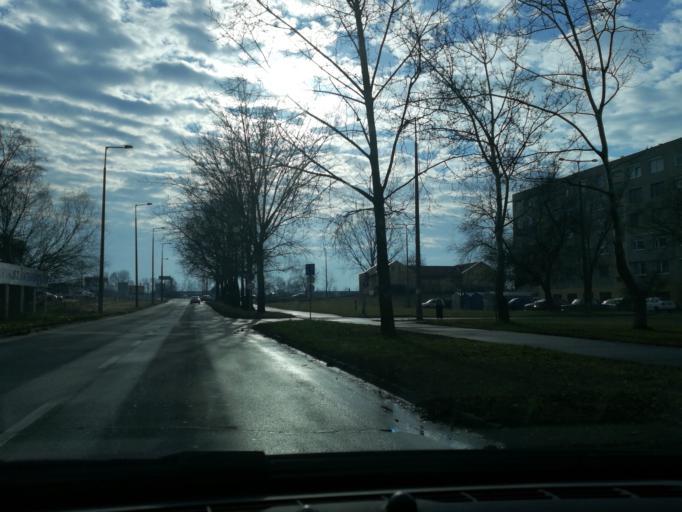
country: HU
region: Szabolcs-Szatmar-Bereg
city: Nyiregyhaza
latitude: 47.9569
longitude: 21.7439
